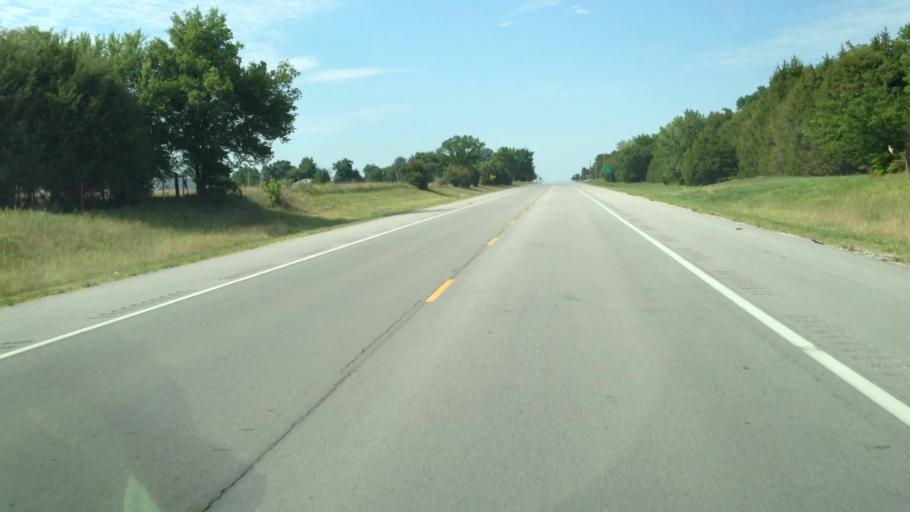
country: US
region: Kansas
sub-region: Labette County
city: Parsons
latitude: 37.3031
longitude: -95.2675
